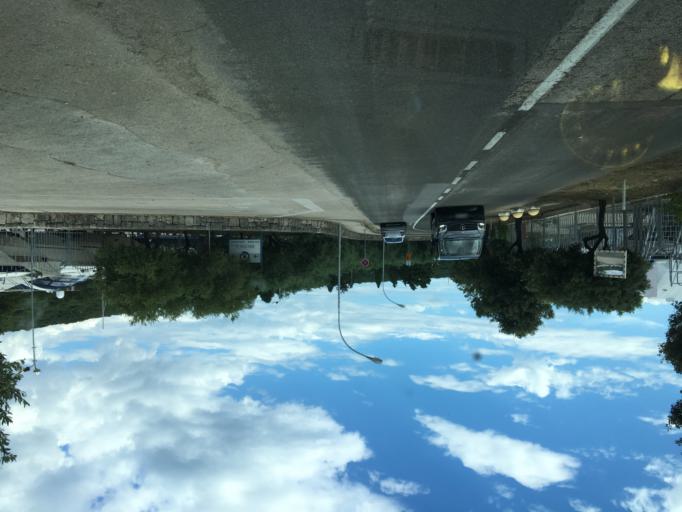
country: HR
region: Primorsko-Goranska
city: Punat
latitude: 45.0316
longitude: 14.6294
